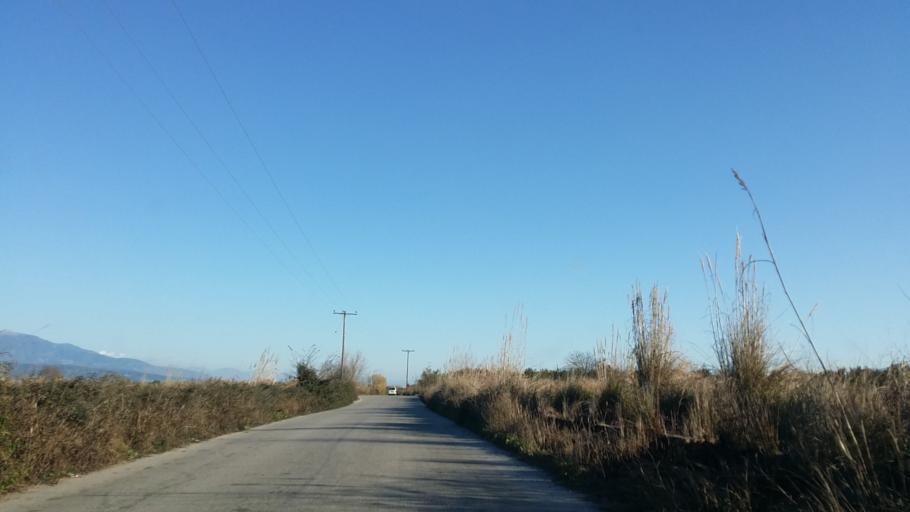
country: GR
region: West Greece
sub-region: Nomos Aitolias kai Akarnanias
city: Lepenou
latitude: 38.6472
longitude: 21.2569
